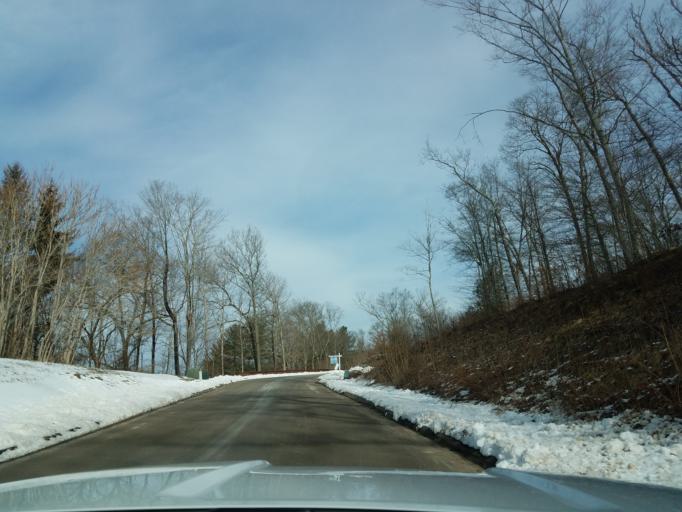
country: US
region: Connecticut
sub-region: New Haven County
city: Guilford
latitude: 41.3525
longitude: -72.6700
